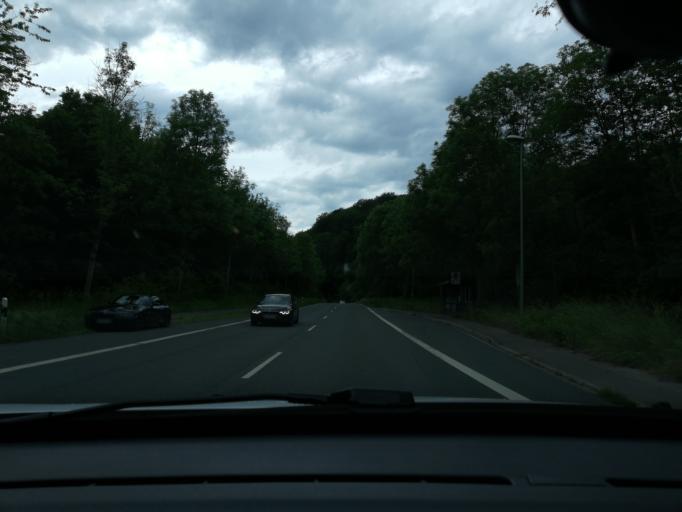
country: DE
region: North Rhine-Westphalia
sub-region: Regierungsbezirk Arnsberg
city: Schalksmuhle
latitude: 51.2834
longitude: 7.5301
